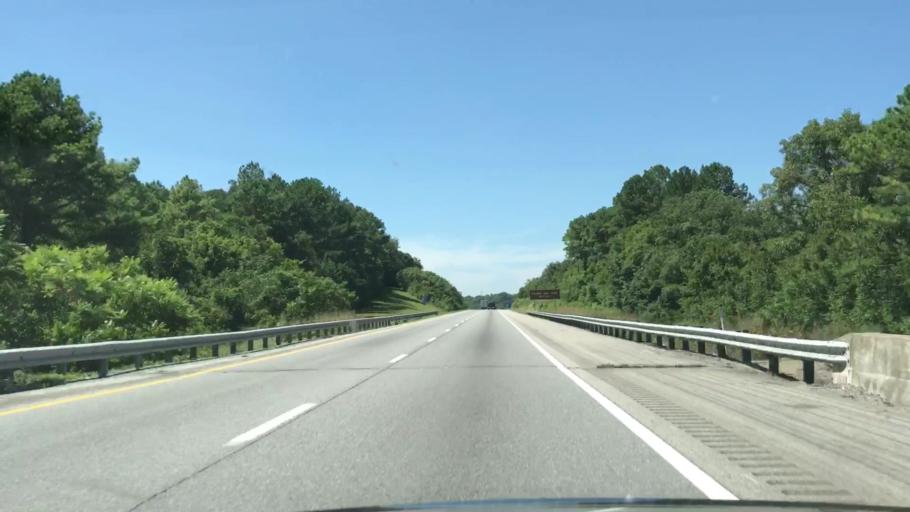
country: US
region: Tennessee
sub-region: Smith County
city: Gordonsville
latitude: 36.1719
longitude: -85.9105
